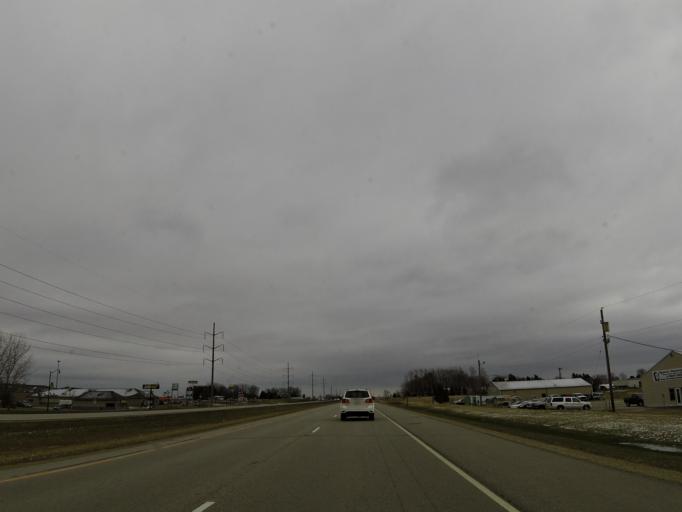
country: US
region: Minnesota
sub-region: Olmsted County
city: Byron
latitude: 44.0286
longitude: -92.6352
